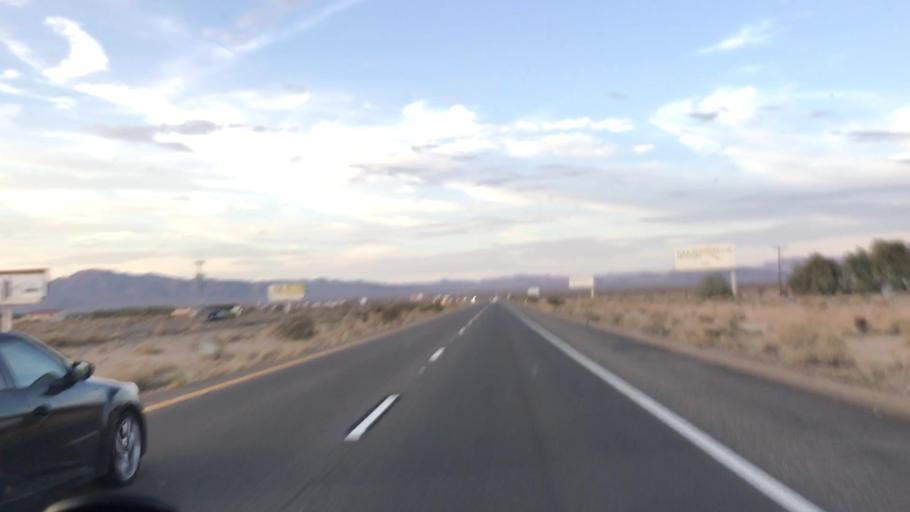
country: US
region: California
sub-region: San Bernardino County
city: Fort Irwin
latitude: 35.2683
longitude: -116.0652
